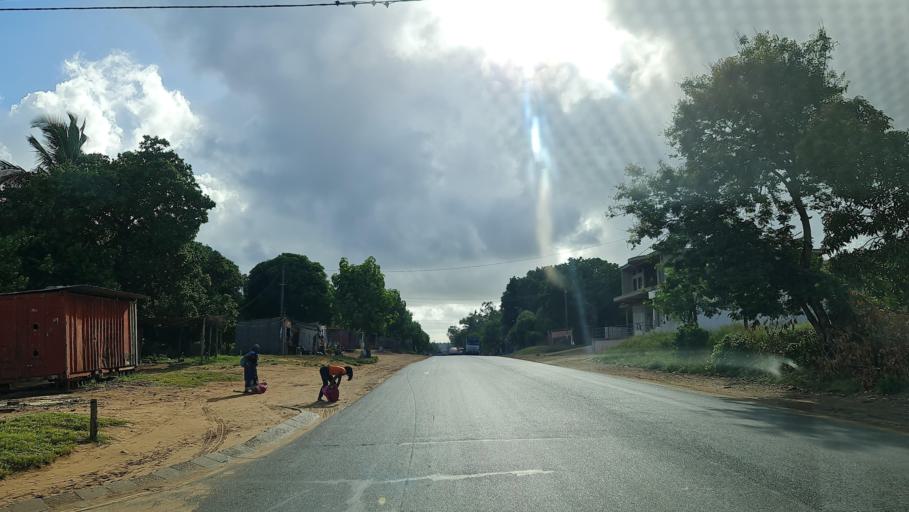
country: MZ
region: Gaza
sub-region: Xai-Xai District
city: Xai-Xai
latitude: -25.0559
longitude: 33.6892
